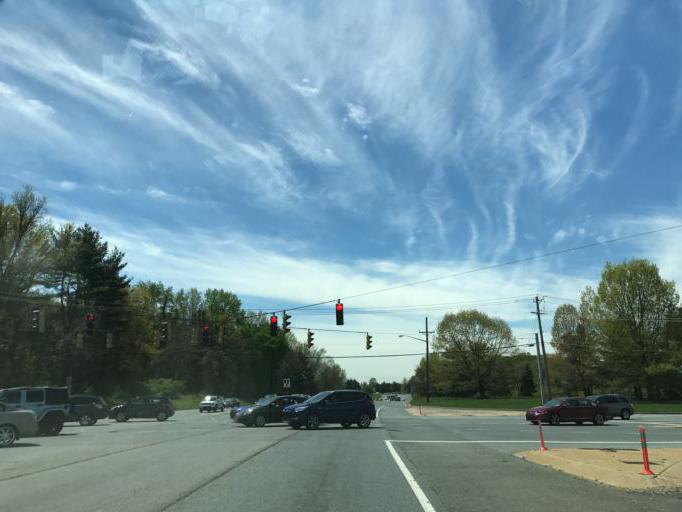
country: US
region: Delaware
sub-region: New Castle County
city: Elsmere
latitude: 39.7591
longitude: -75.6041
